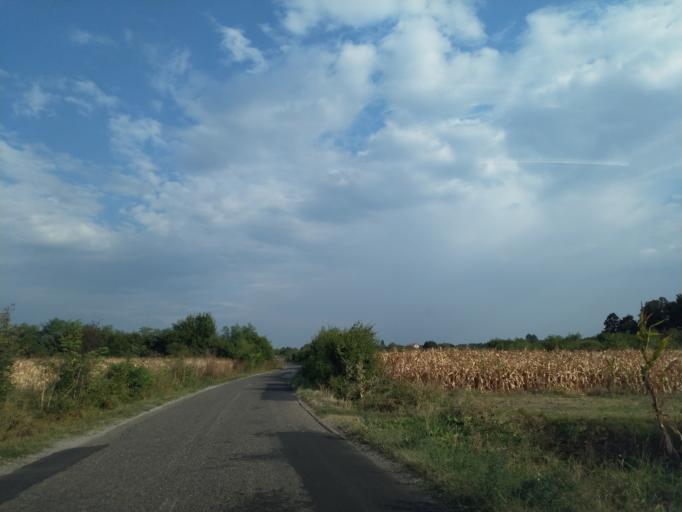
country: RS
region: Central Serbia
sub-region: Pomoravski Okrug
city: Paracin
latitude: 43.8482
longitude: 21.4632
